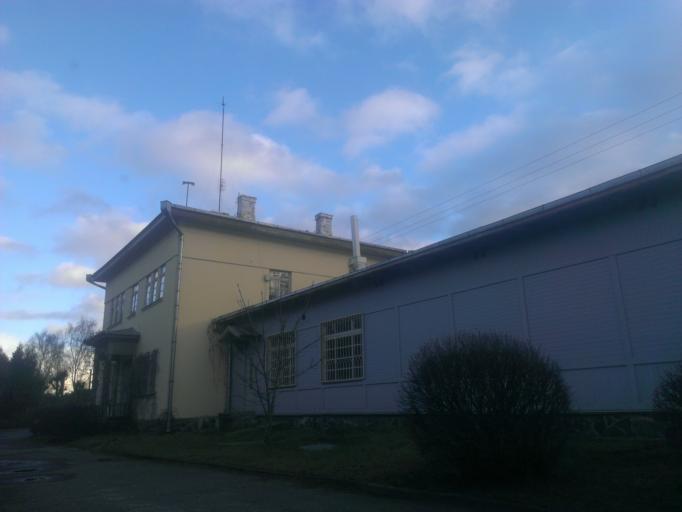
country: LV
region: Riga
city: Jaunciems
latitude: 57.0745
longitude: 24.1140
